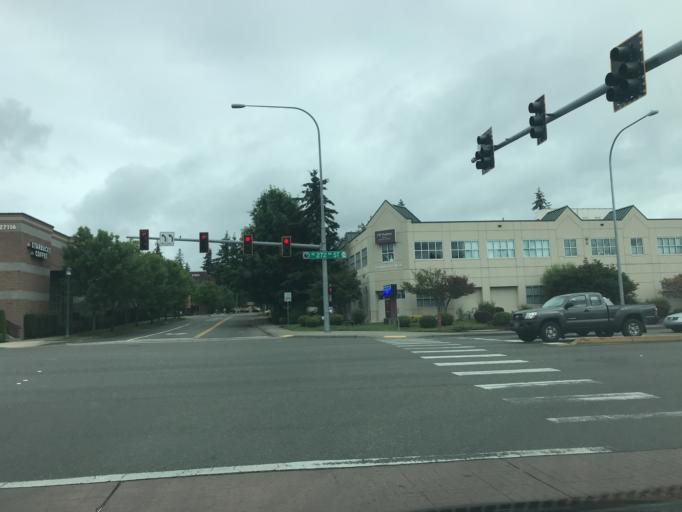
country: US
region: Washington
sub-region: King County
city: Covington
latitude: 47.3579
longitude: -122.1170
